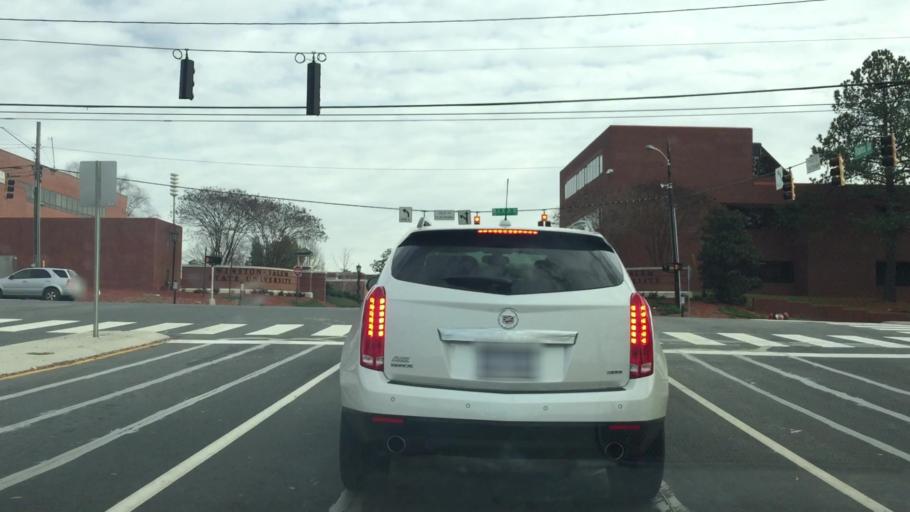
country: US
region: North Carolina
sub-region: Forsyth County
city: Winston-Salem
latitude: 36.0905
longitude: -80.2281
